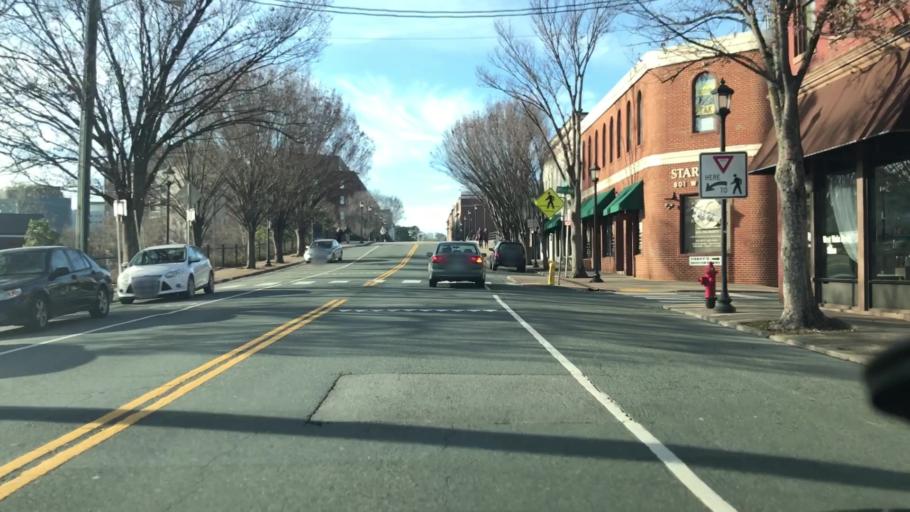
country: US
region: Virginia
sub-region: City of Charlottesville
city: Charlottesville
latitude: 38.0317
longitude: -78.4906
